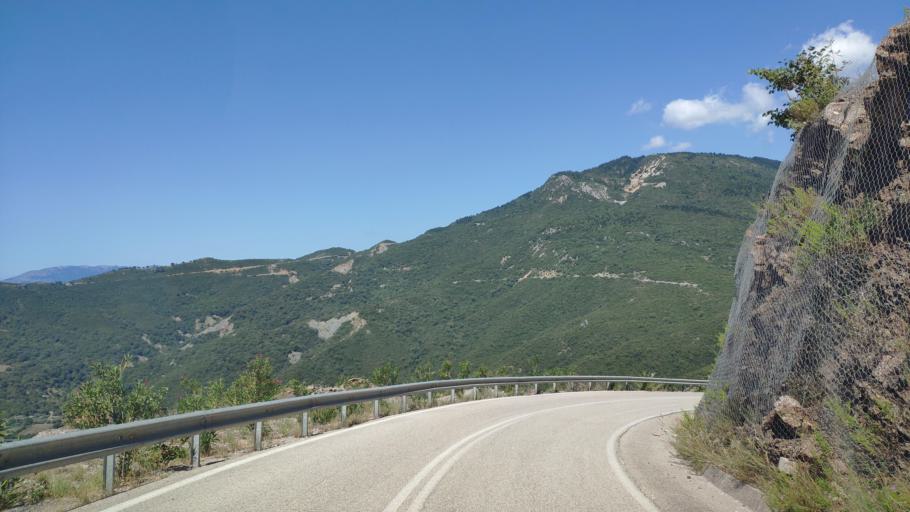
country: GR
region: Central Greece
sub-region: Nomos Evrytanias
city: Kerasochori
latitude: 39.0138
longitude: 21.5973
